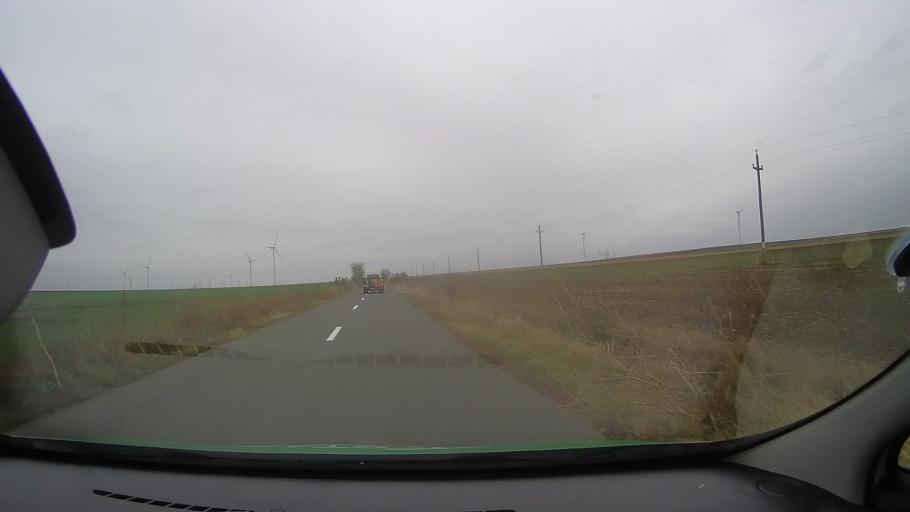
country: RO
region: Constanta
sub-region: Comuna Targusor
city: Targusor
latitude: 44.4729
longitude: 28.3846
